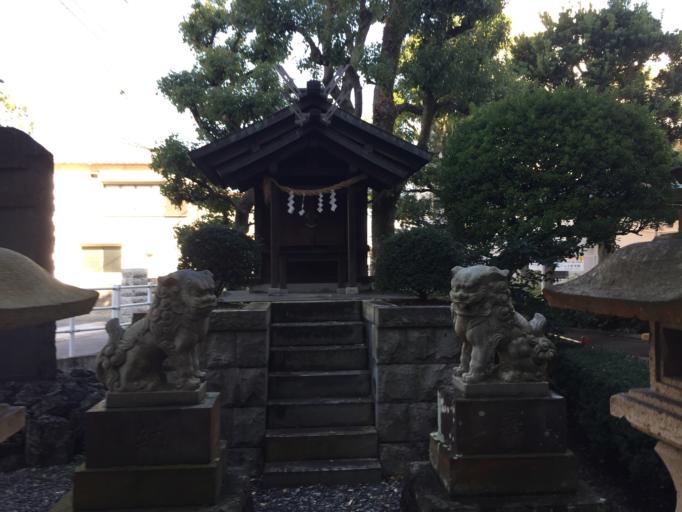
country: JP
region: Shizuoka
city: Numazu
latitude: 35.1088
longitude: 138.8575
